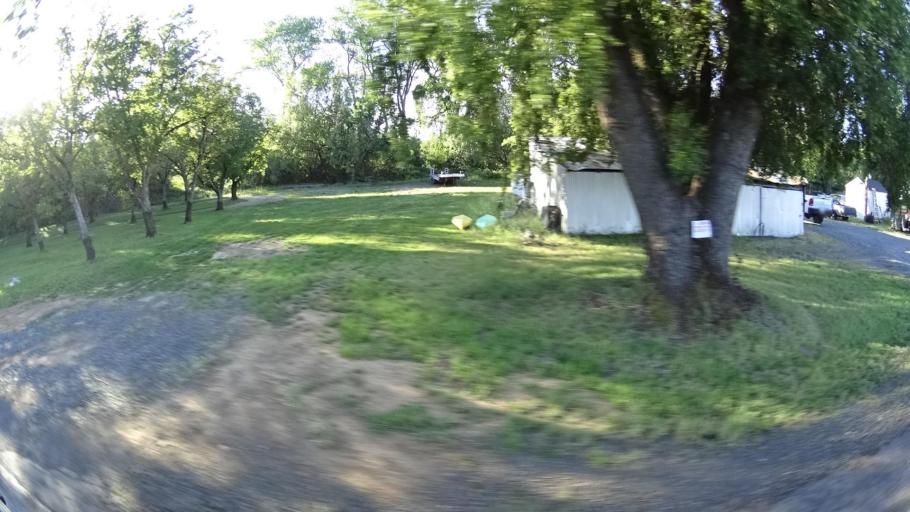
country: US
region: California
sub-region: Lake County
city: Upper Lake
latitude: 39.1735
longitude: -122.9040
